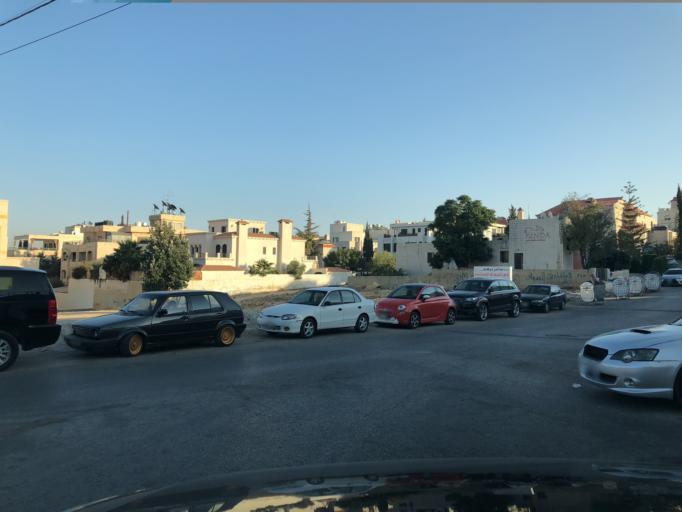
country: JO
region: Amman
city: Al Bunayyat ash Shamaliyah
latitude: 31.9410
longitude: 35.8849
